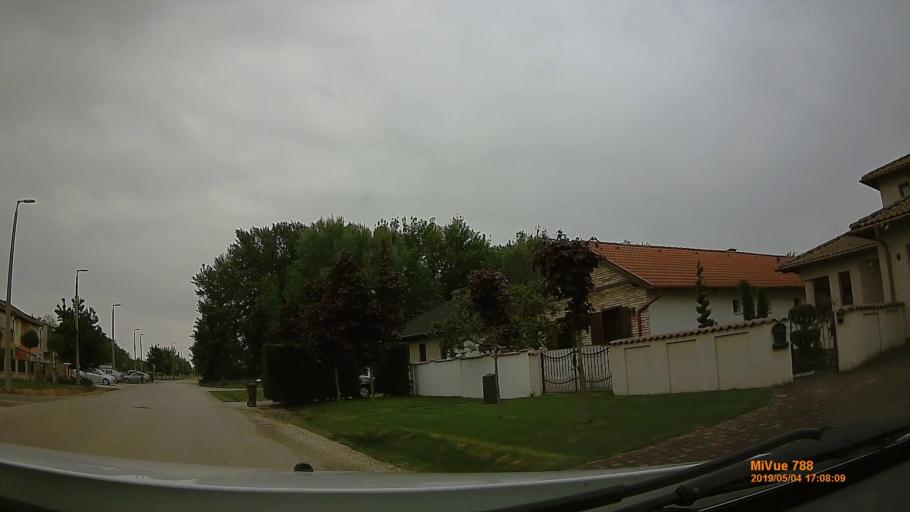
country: HU
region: Gyor-Moson-Sopron
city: Mosonmagyarovar
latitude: 47.8890
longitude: 17.2893
